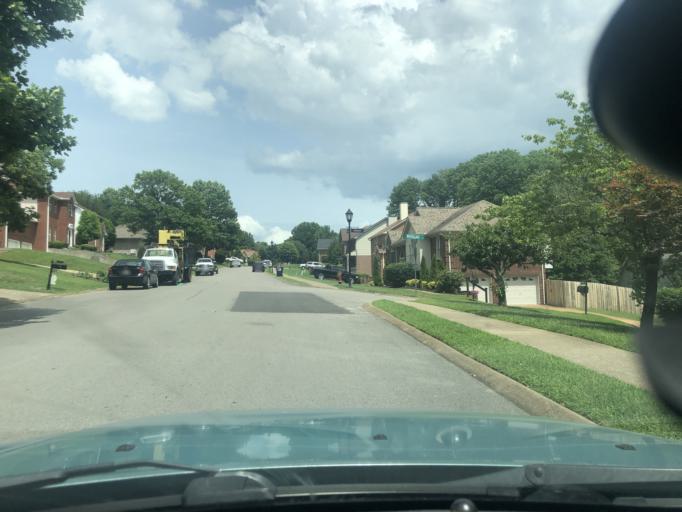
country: US
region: Tennessee
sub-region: Davidson County
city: Lakewood
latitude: 36.1328
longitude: -86.6336
